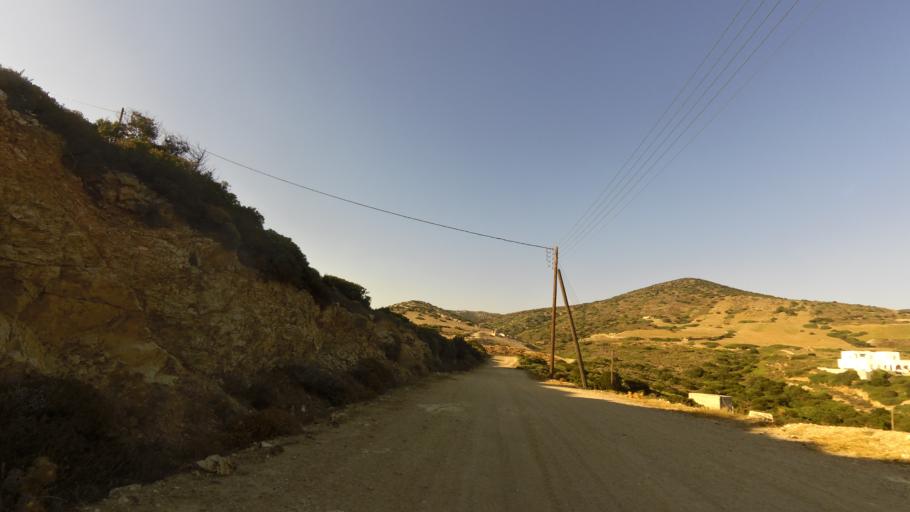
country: GR
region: South Aegean
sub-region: Nomos Kykladon
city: Antiparos
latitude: 36.9809
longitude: 25.0283
